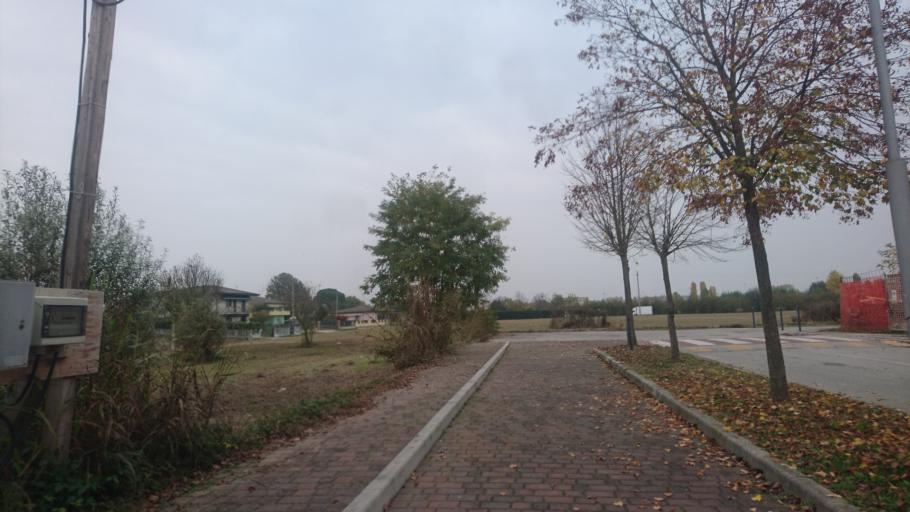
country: IT
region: Veneto
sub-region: Provincia di Venezia
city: Tombelle
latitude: 45.3974
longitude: 11.9866
